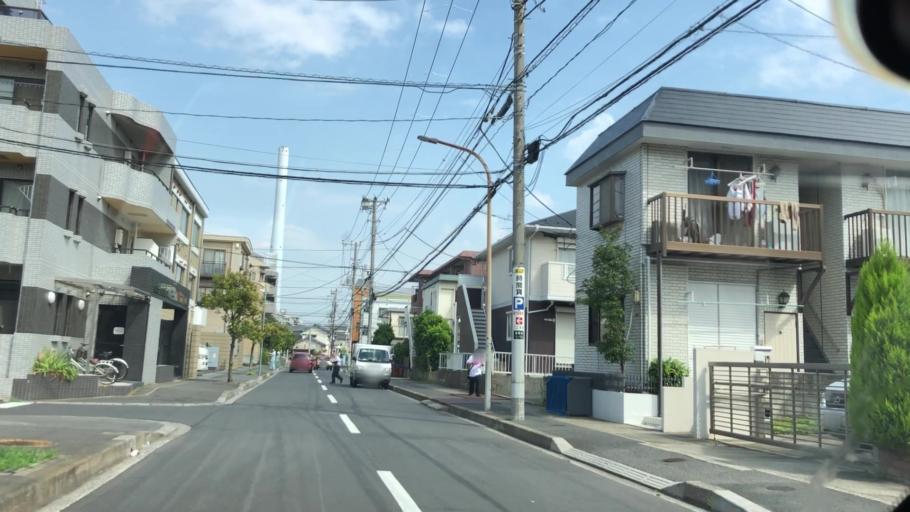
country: JP
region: Tokyo
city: Urayasu
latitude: 35.6803
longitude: 139.9092
